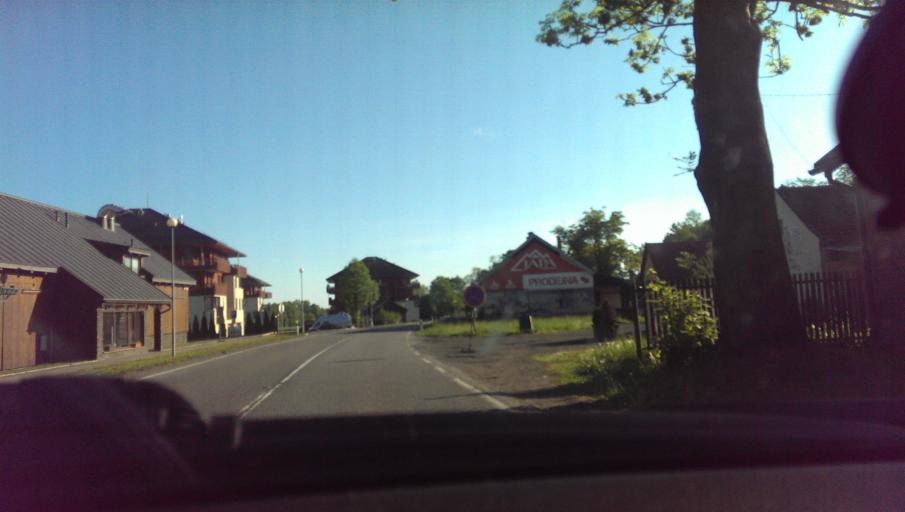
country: CZ
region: Moravskoslezsky
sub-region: Okres Frydek-Mistek
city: Celadna
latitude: 49.5514
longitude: 18.3406
